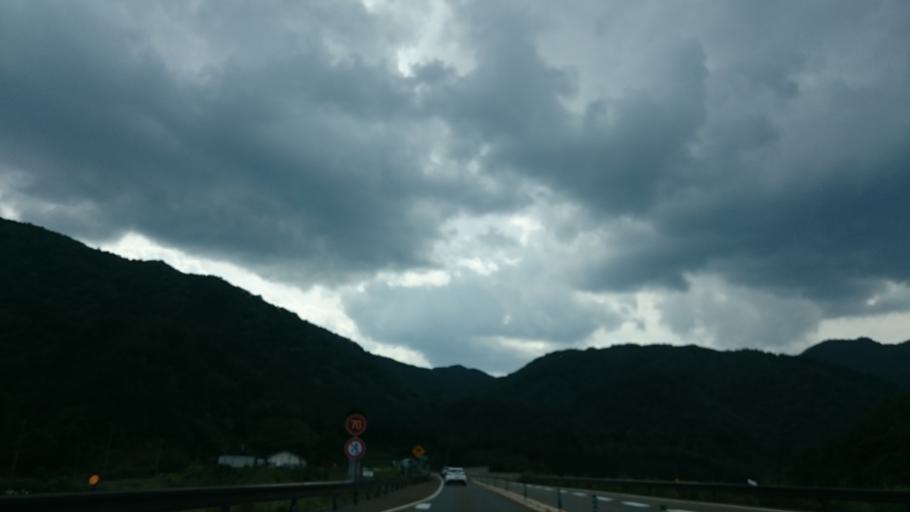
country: JP
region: Gifu
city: Takayama
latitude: 36.1407
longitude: 137.1440
